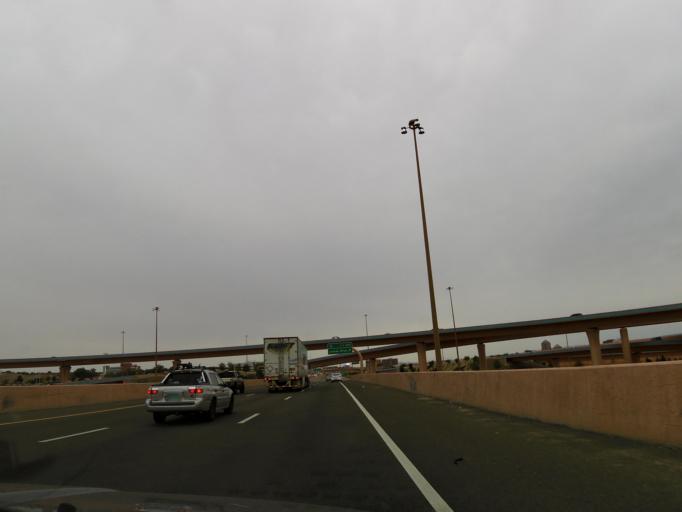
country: US
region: New Mexico
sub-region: Bernalillo County
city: Albuquerque
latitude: 35.1062
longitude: -106.6287
